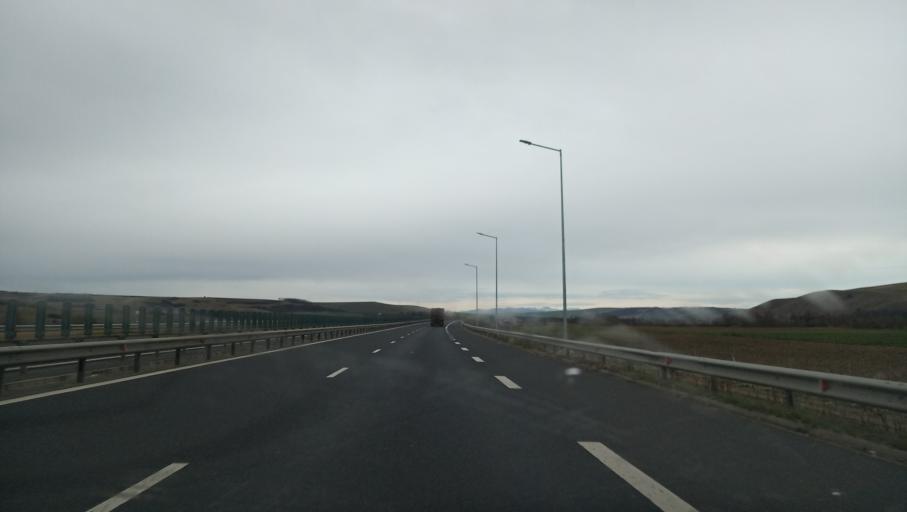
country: RO
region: Alba
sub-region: Comuna Garbova
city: Garbova
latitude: 45.9027
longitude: 23.7551
